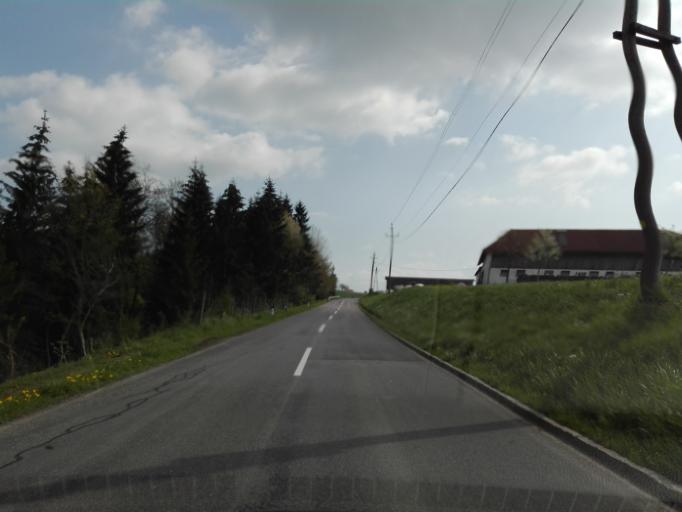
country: AT
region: Upper Austria
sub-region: Politischer Bezirk Perg
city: Perg
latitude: 48.2759
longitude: 14.6614
